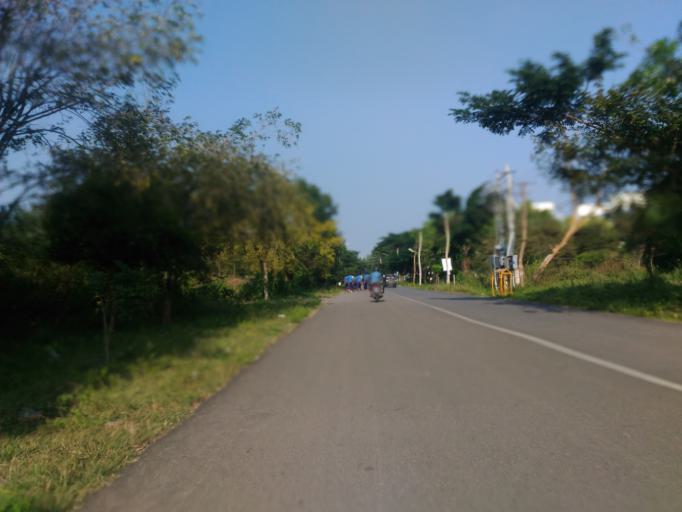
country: IN
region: Karnataka
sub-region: Bangalore Urban
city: Bangalore
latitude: 12.9406
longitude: 77.5035
